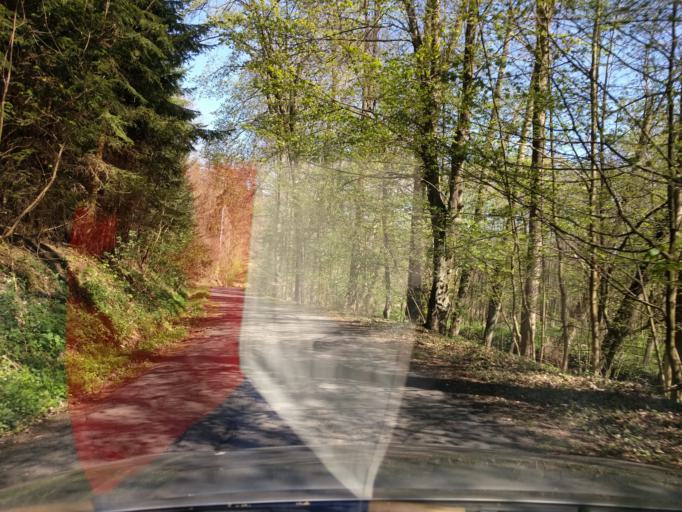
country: CZ
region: Central Bohemia
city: Kostelec nad Cernymi Lesy
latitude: 50.0328
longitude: 14.8281
